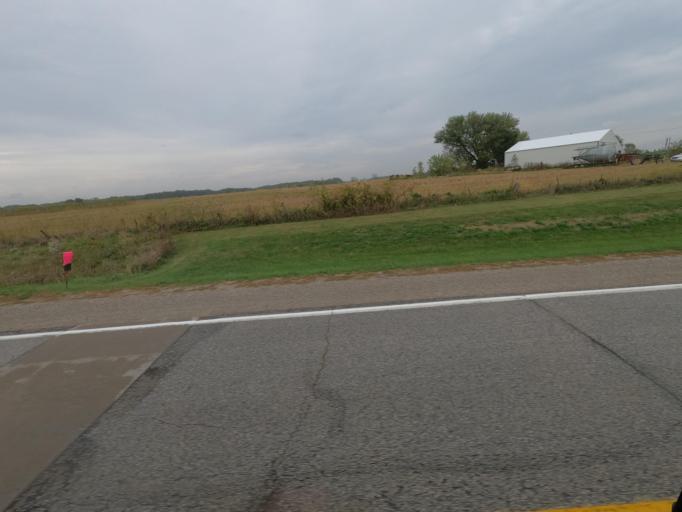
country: US
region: Iowa
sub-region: Van Buren County
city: Keosauqua
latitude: 40.8496
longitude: -92.0357
